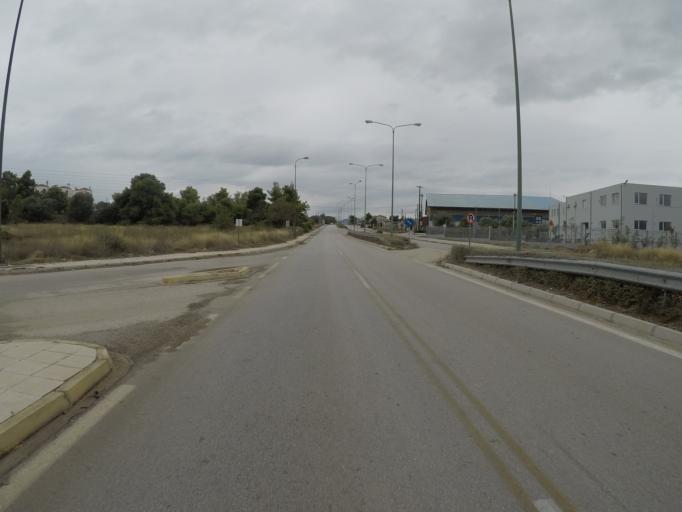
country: GR
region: Peloponnese
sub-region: Nomos Korinthias
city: Korinthos
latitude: 37.9462
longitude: 22.9794
